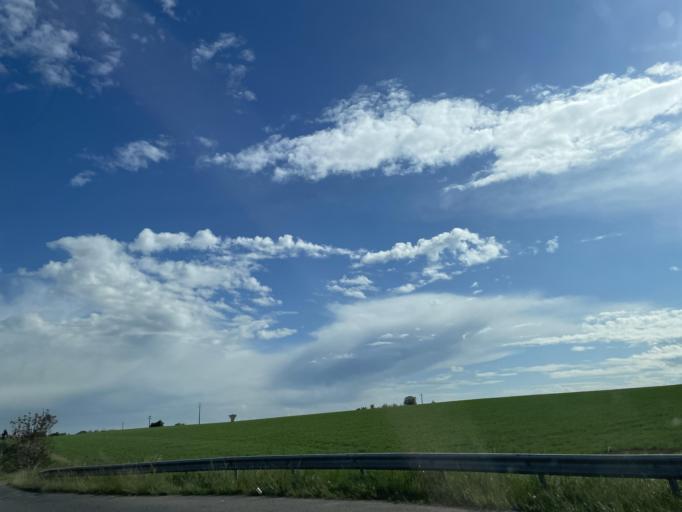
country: FR
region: Ile-de-France
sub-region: Departement de Seine-et-Marne
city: Charny
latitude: 48.9501
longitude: 2.7729
